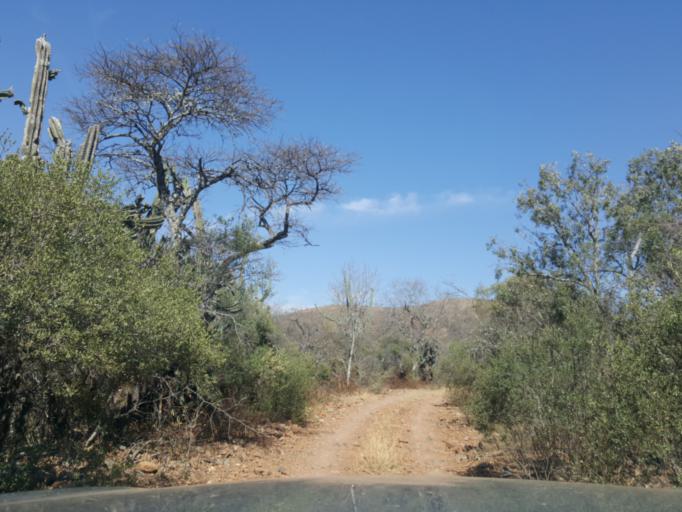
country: BW
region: South East
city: Lobatse
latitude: -25.1579
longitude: 25.6846
